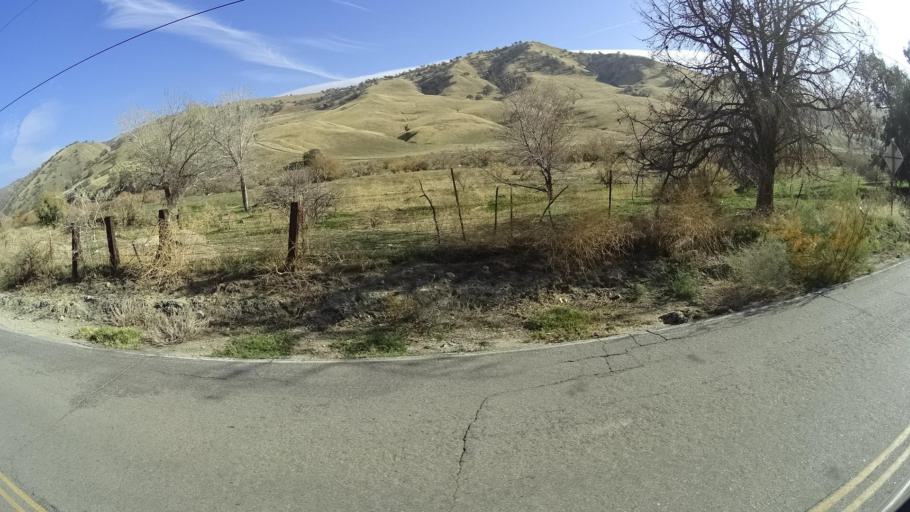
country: US
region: California
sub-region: Kern County
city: Bear Valley Springs
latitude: 35.2950
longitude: -118.6153
